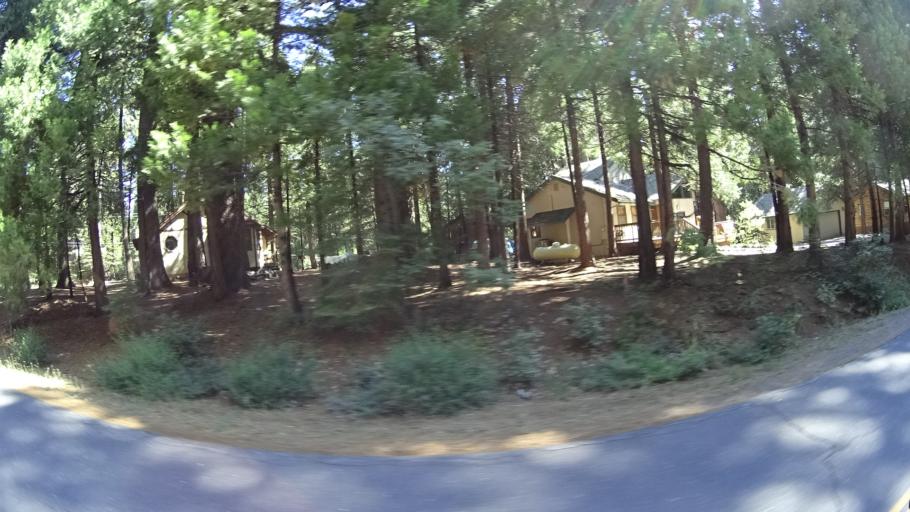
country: US
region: California
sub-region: Calaveras County
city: Arnold
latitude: 38.2907
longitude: -120.2801
